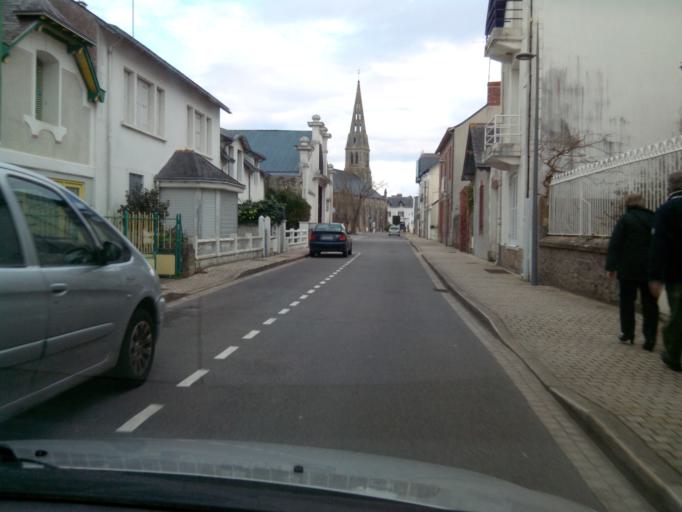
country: FR
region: Pays de la Loire
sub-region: Departement de la Loire-Atlantique
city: Le Pouliguen
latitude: 47.2750
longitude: -2.4306
